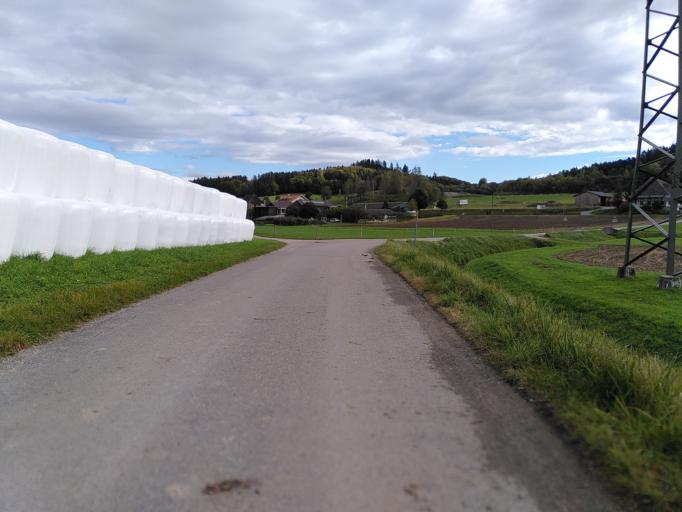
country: CH
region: Bern
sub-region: Emmental District
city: Wynigen
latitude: 47.1009
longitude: 7.6391
